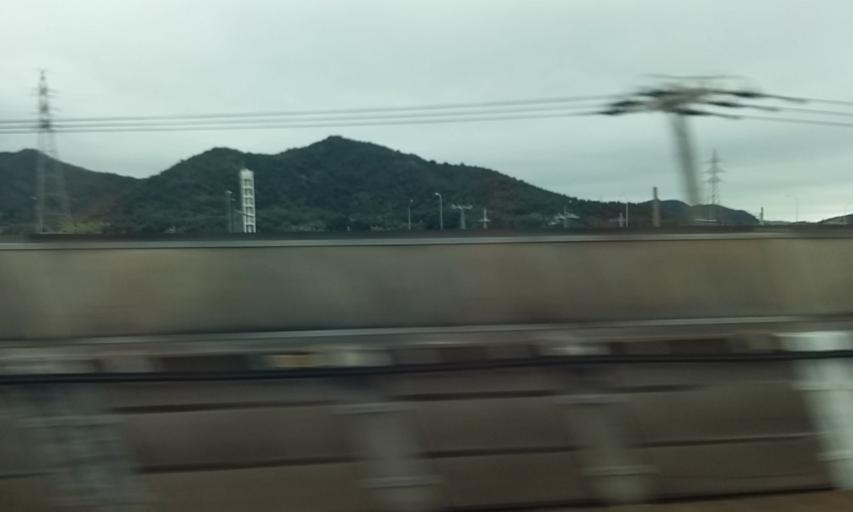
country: JP
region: Hyogo
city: Shirahamacho-usazakiminami
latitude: 34.7931
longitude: 134.7632
